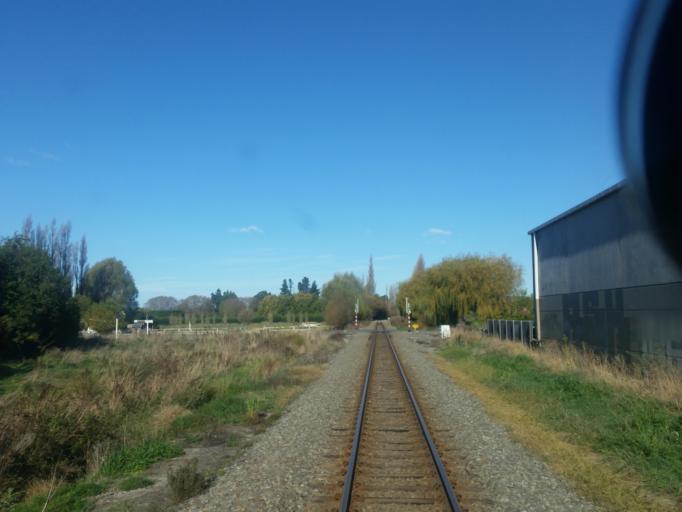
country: NZ
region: Canterbury
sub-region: Waimakariri District
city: Woodend
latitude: -43.3165
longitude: 172.6015
